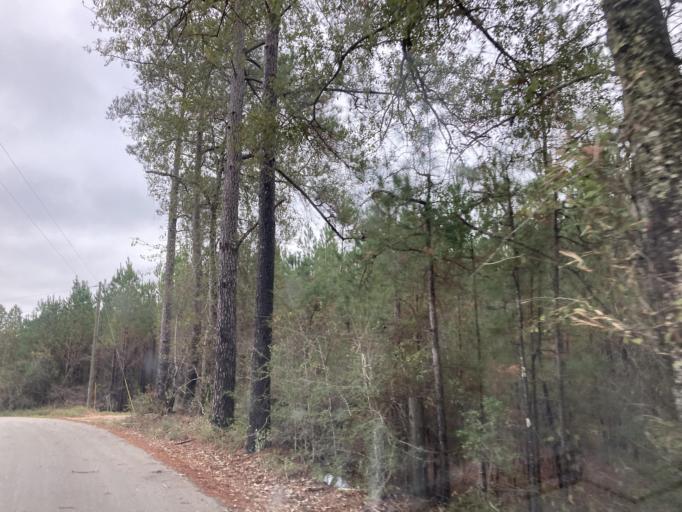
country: US
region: Mississippi
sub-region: Lamar County
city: Purvis
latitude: 31.1869
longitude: -89.4268
